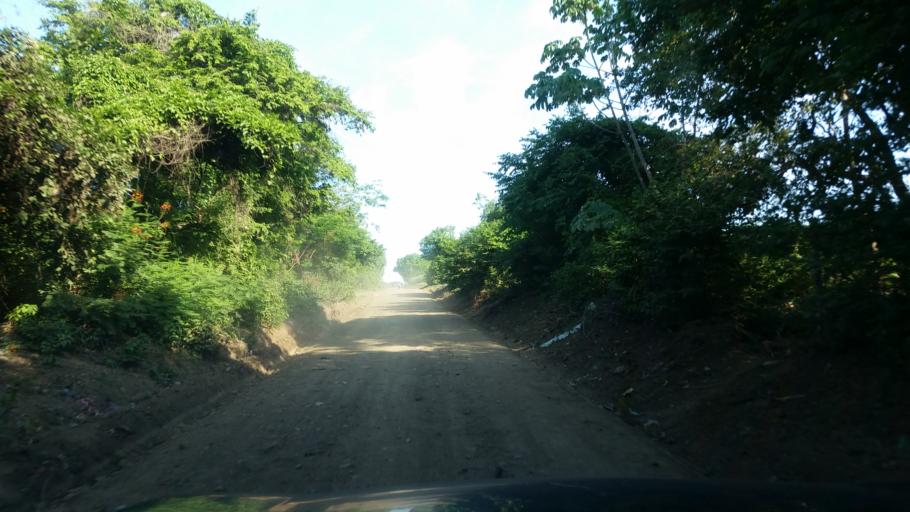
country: NI
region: Managua
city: Masachapa
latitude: 11.7951
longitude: -86.5058
